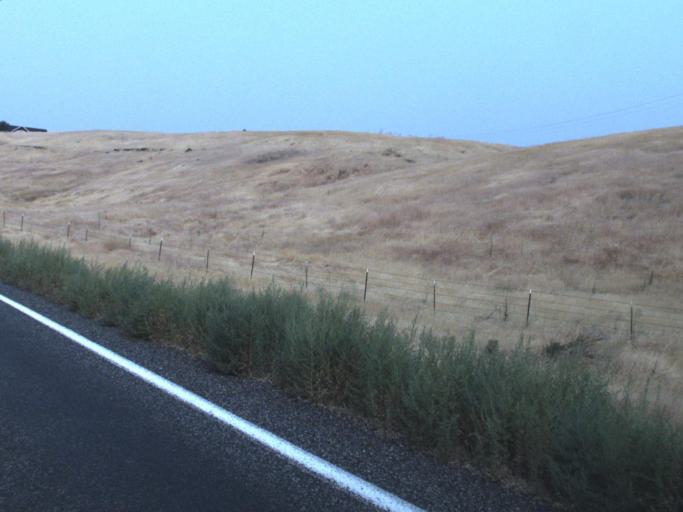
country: US
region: Washington
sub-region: Grant County
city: Desert Aire
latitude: 46.5273
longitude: -119.8749
